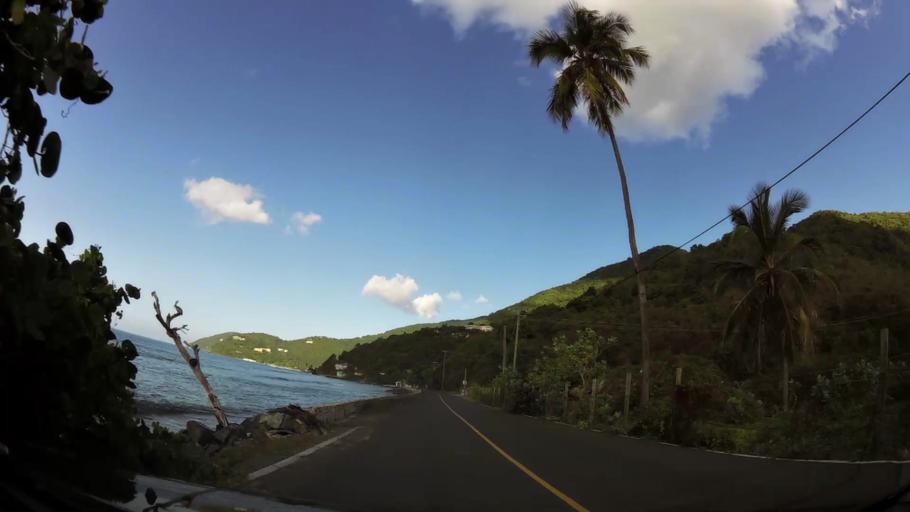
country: VG
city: Road Town
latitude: 18.4002
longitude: -64.6794
